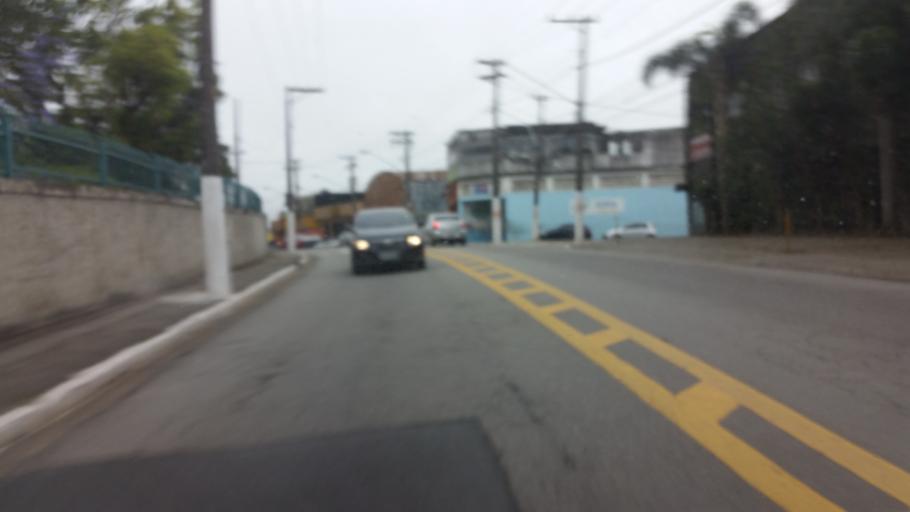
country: BR
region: Sao Paulo
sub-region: Diadema
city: Diadema
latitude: -23.6382
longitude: -46.6135
